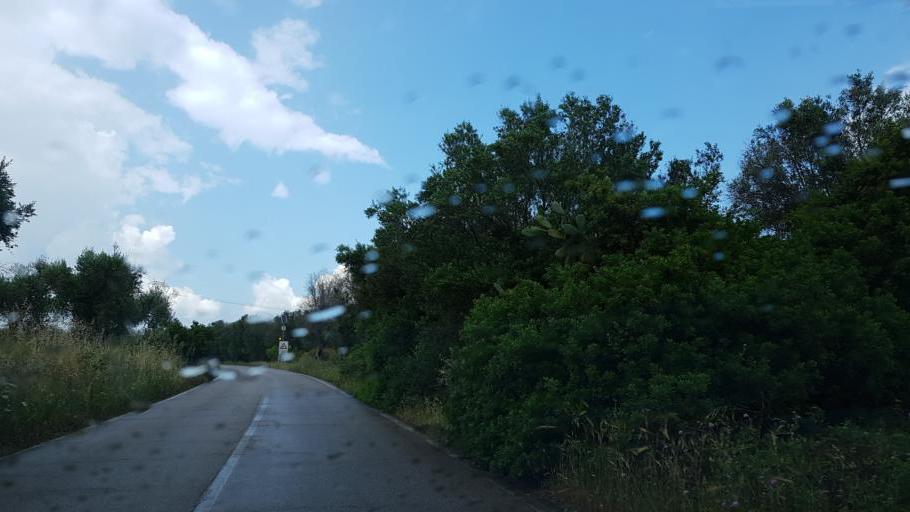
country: IT
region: Apulia
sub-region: Provincia di Brindisi
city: Cellino San Marco
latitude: 40.4750
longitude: 17.9372
